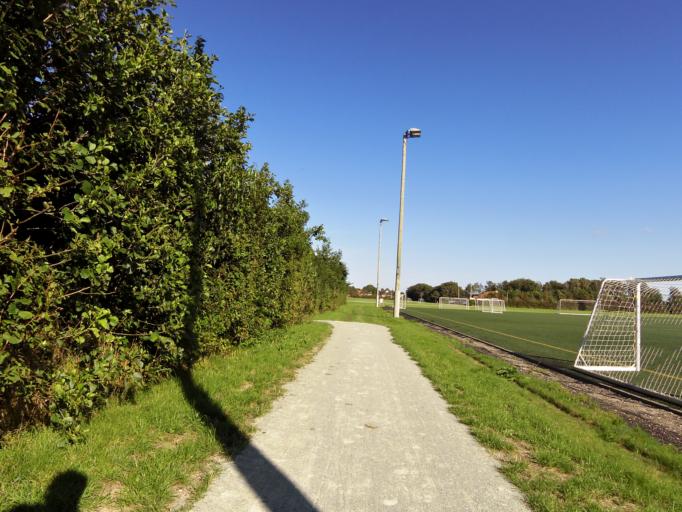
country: DK
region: South Denmark
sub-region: Tonder Kommune
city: Sherrebek
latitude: 55.1573
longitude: 8.7551
